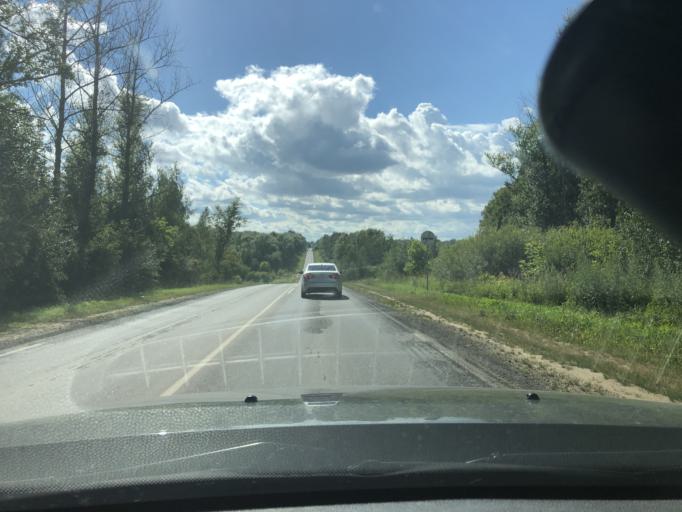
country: RU
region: Tula
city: Donskoy
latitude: 53.9693
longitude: 38.3898
